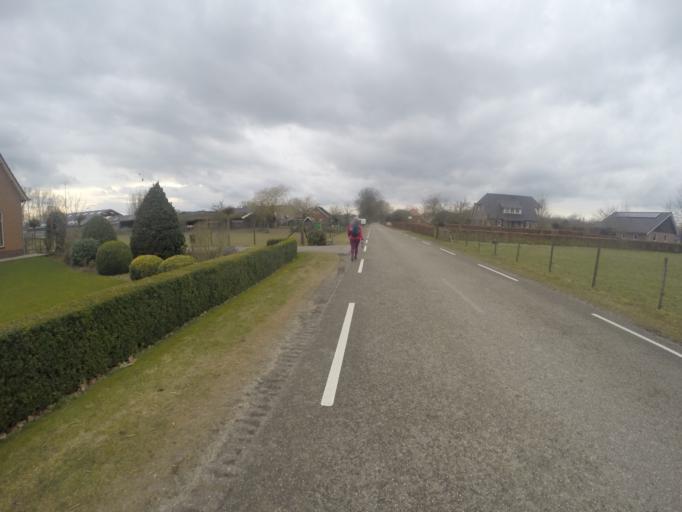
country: NL
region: Gelderland
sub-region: Gemeente Bronckhorst
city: Hengelo
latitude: 52.0485
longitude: 6.3280
